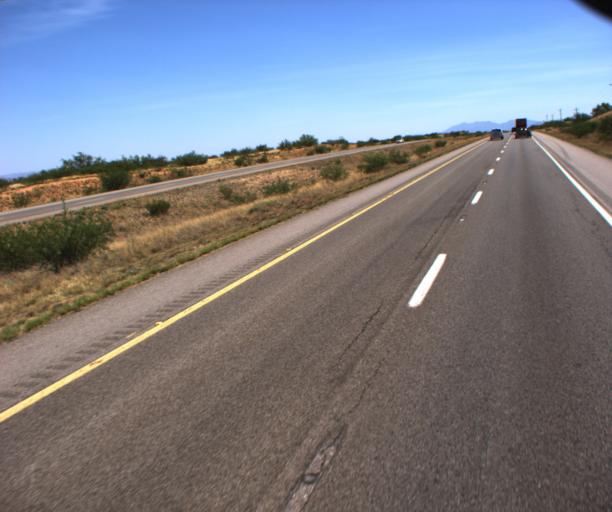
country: US
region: Arizona
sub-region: Cochise County
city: Whetstone
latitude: 31.8784
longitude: -110.3413
